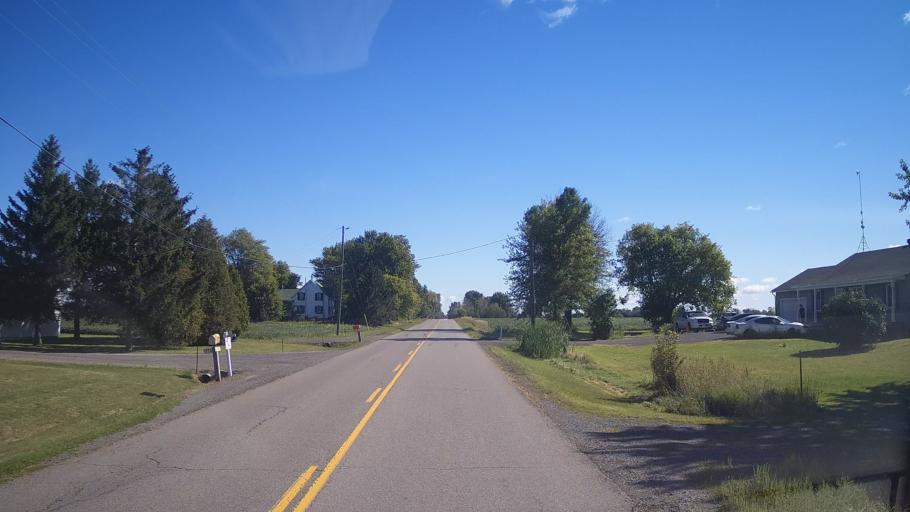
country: CA
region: Ontario
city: Prescott
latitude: 44.9175
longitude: -75.3620
